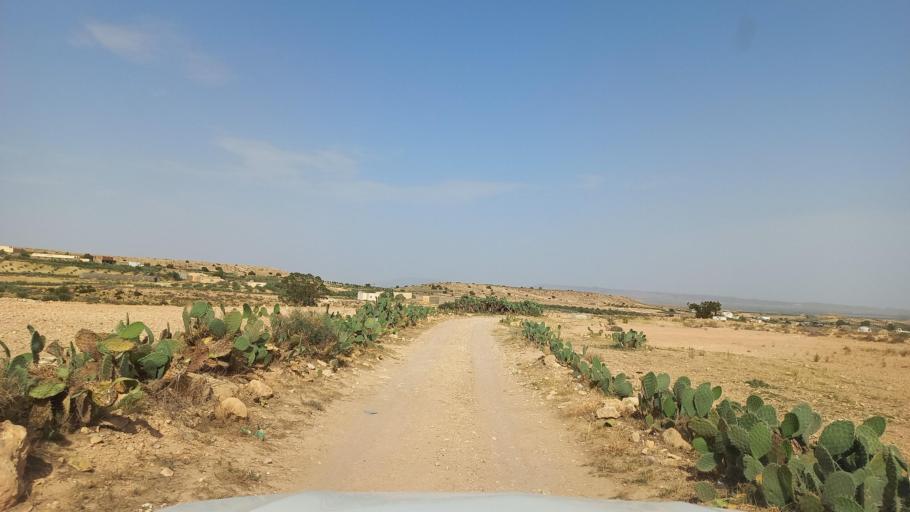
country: TN
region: Al Qasrayn
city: Kasserine
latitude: 35.3034
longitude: 8.9387
